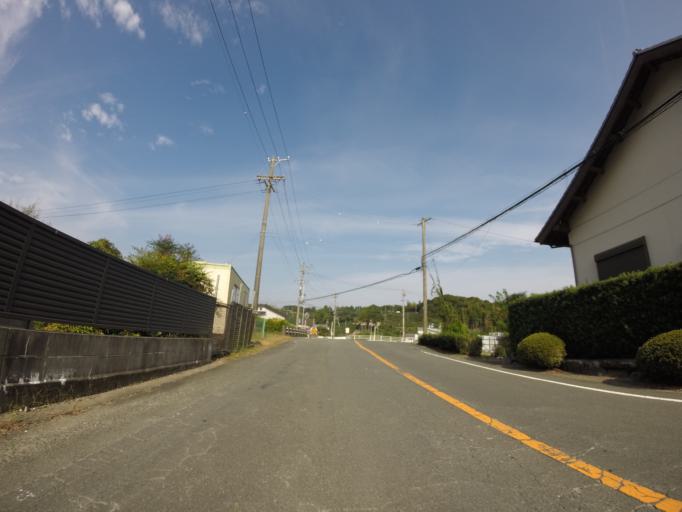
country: JP
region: Shizuoka
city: Shimada
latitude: 34.7528
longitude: 138.1978
